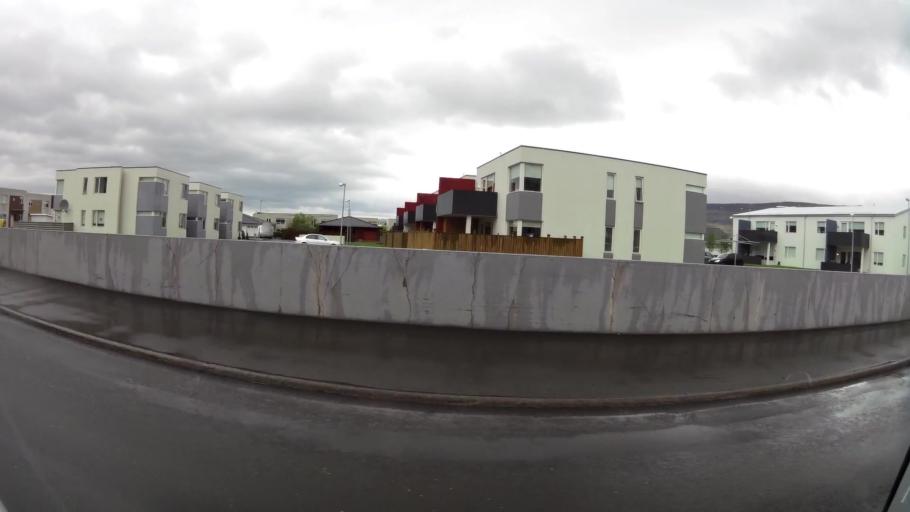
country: IS
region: Northeast
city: Akureyri
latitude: 65.6658
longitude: -18.1029
